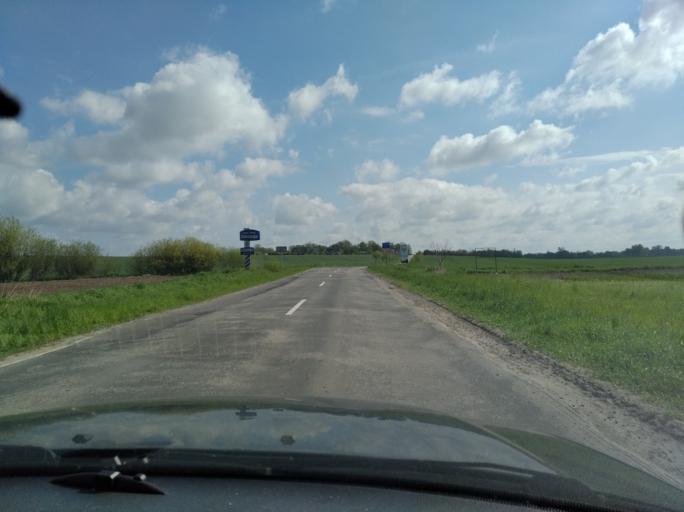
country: PL
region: Subcarpathian Voivodeship
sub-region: Powiat przeworski
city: Kanczuga
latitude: 49.9999
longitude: 22.4298
